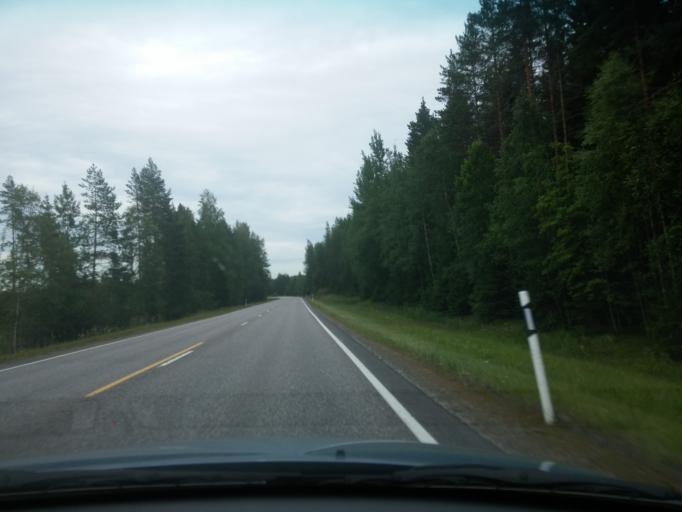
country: FI
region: Haeme
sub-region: Riihimaeki
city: Loppi
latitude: 60.7343
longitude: 24.3849
